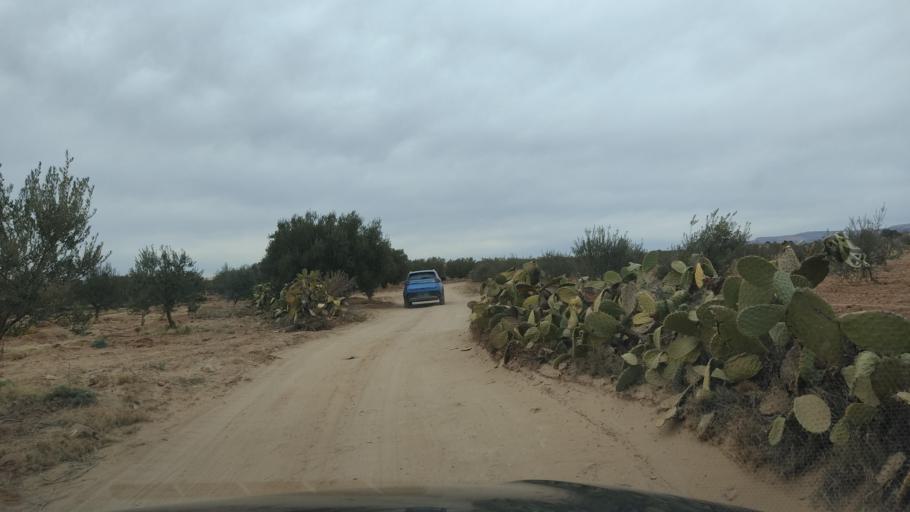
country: TN
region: Al Qasrayn
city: Kasserine
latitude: 35.2273
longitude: 8.9171
